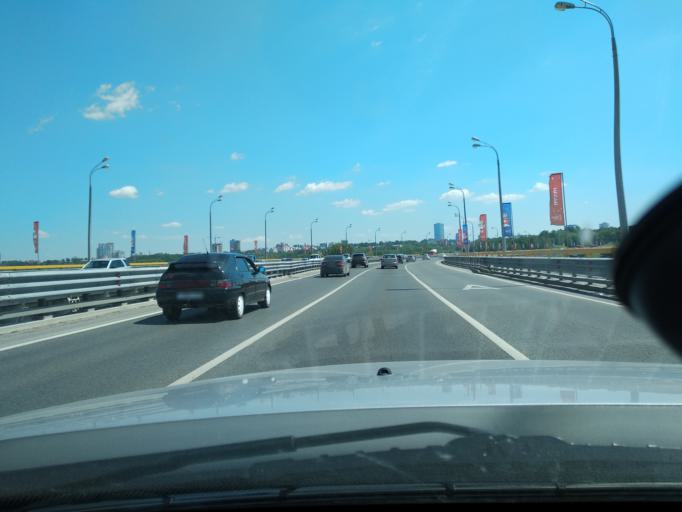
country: RU
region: Tatarstan
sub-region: Gorod Kazan'
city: Kazan
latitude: 55.8060
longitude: 49.1452
